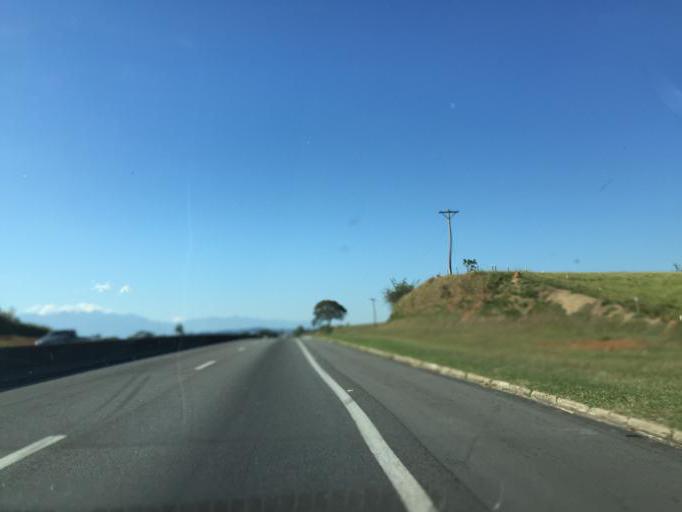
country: BR
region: Sao Paulo
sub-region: Lorena
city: Lorena
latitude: -22.7053
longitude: -45.0413
